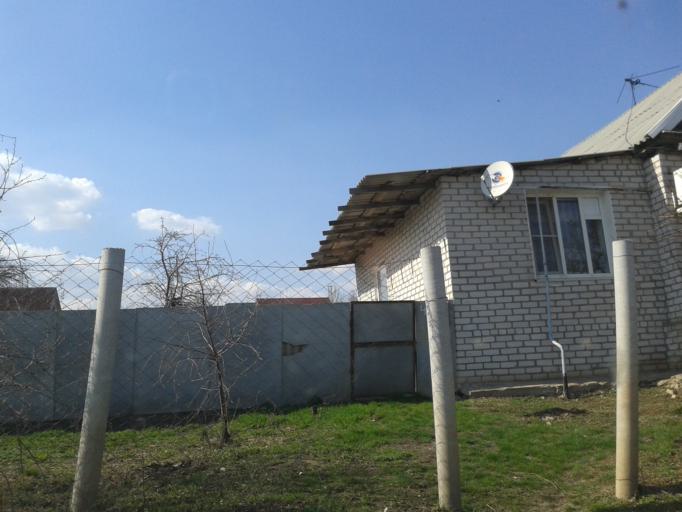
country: RU
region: Volgograd
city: Volgograd
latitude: 48.6277
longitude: 44.3811
